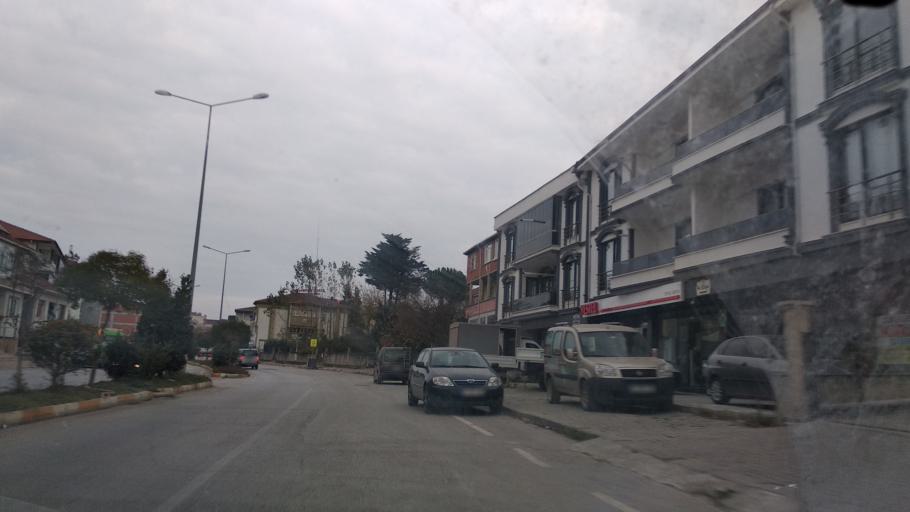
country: TR
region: Sakarya
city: Karasu
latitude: 41.0951
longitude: 30.6846
